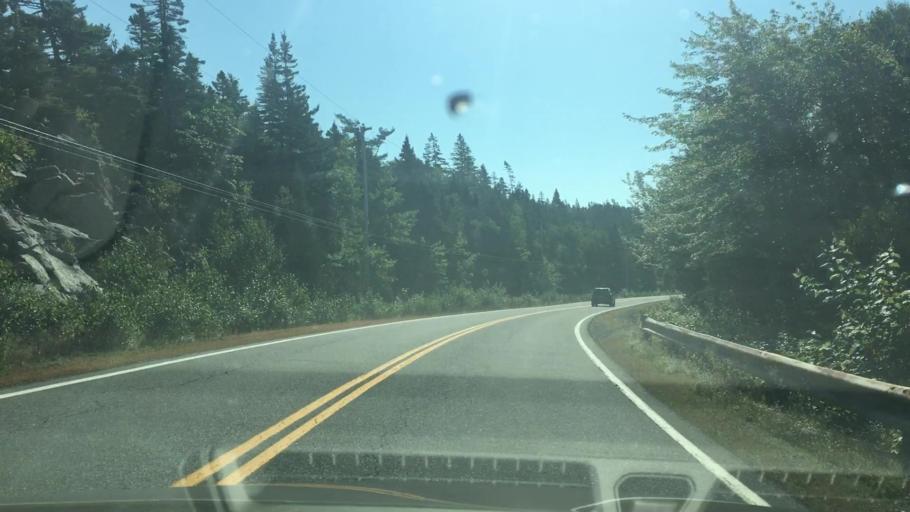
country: CA
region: Nova Scotia
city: Cole Harbour
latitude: 44.8116
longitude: -62.8370
